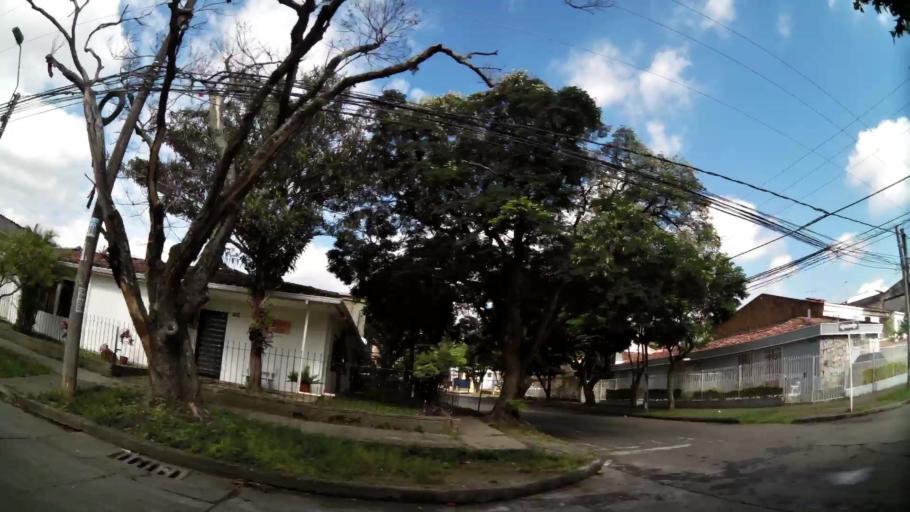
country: CO
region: Valle del Cauca
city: Cali
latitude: 3.4236
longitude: -76.5393
